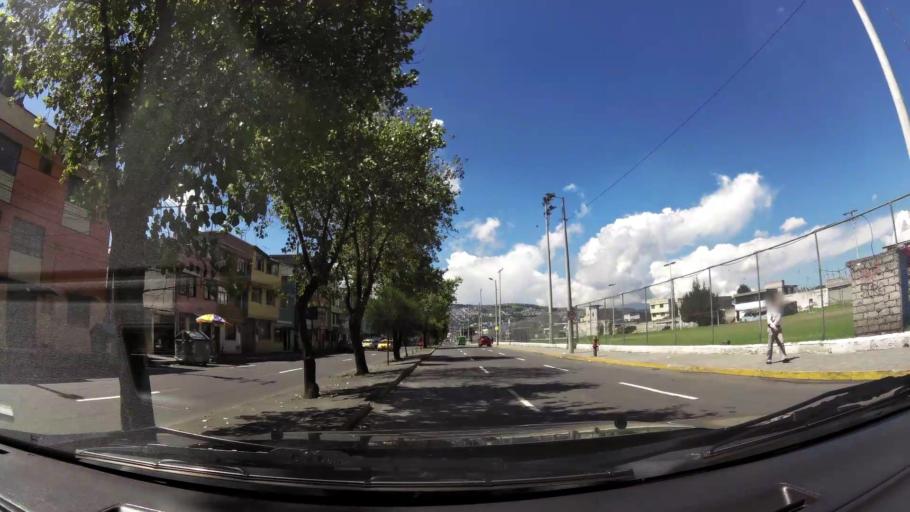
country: EC
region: Pichincha
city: Quito
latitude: -0.2687
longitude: -78.5460
